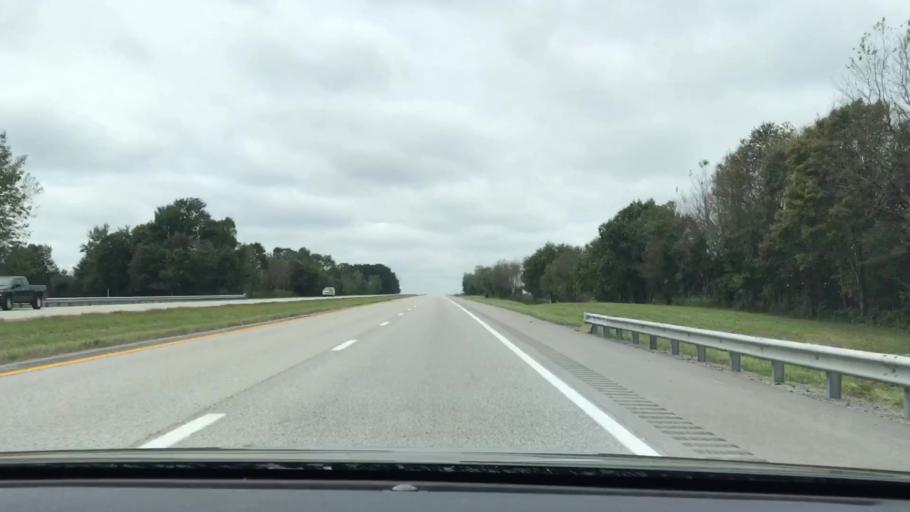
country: US
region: Kentucky
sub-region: Russell County
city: Russell Springs
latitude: 37.0729
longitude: -85.0034
